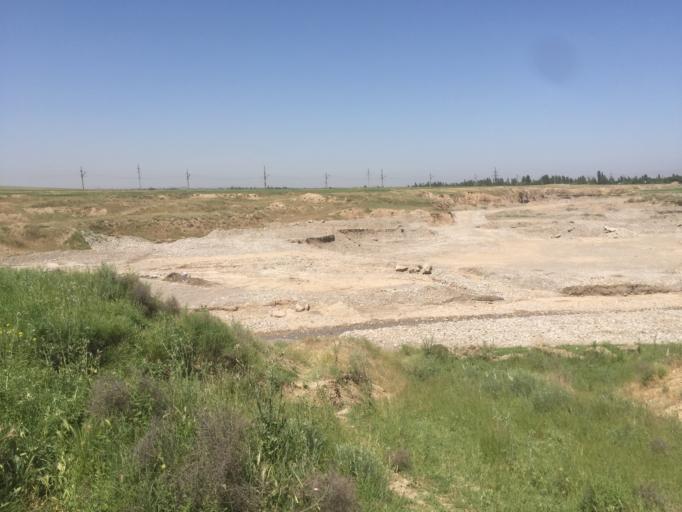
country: TJ
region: Viloyati Sughd
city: Proletar
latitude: 40.0925
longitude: 69.5389
